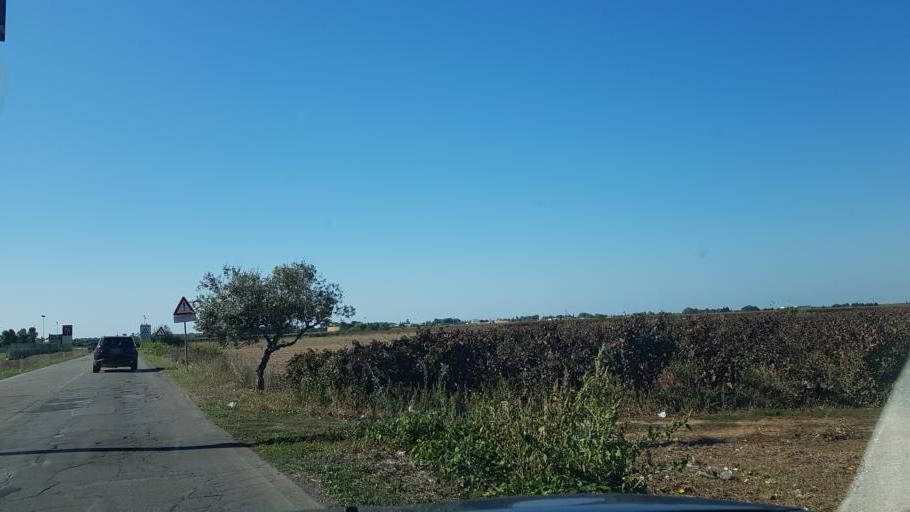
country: IT
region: Apulia
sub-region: Provincia di Lecce
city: Leverano
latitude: 40.2929
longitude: 17.9863
